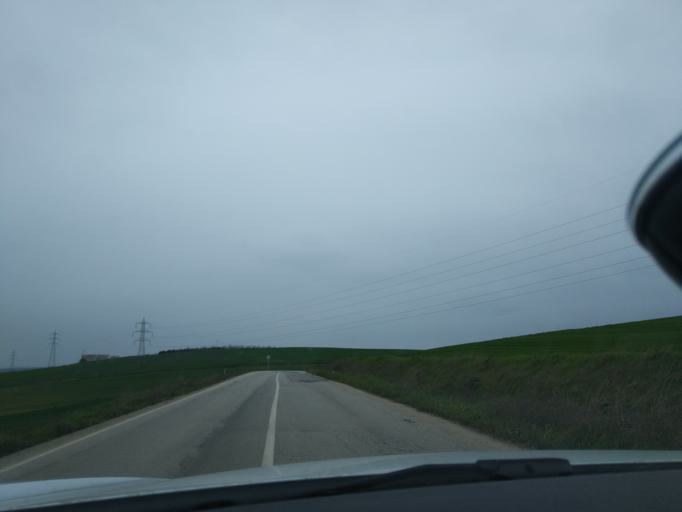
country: TR
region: Tekirdag
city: Marmara Ereglisi
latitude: 41.0287
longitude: 27.8456
